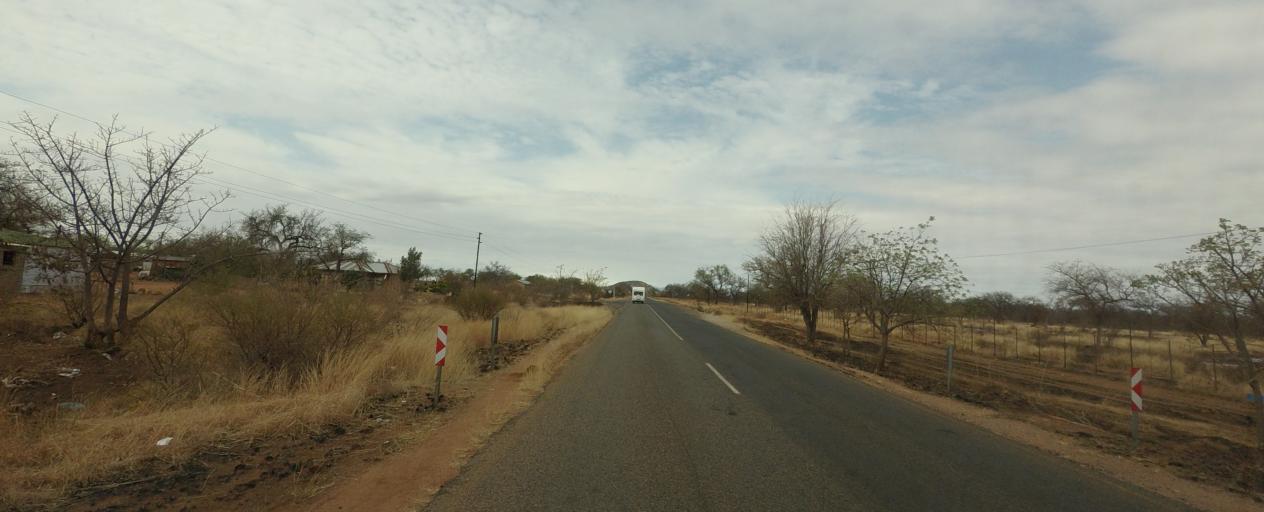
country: BW
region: Central
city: Mathathane
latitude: -22.6629
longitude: 29.1134
